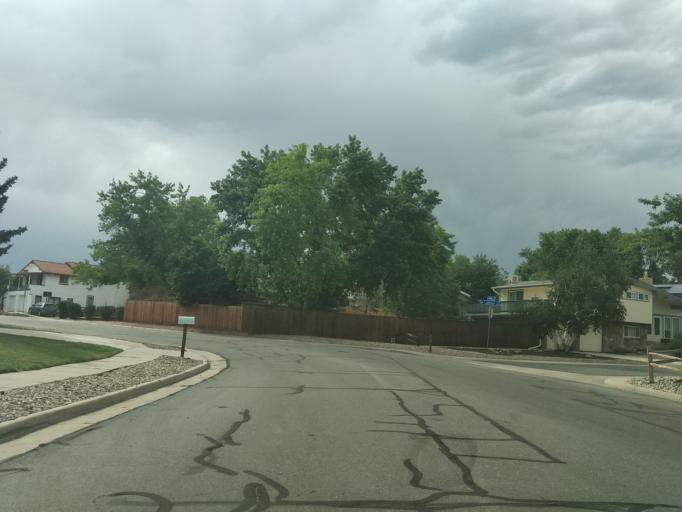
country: US
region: Colorado
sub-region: Jefferson County
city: Lakewood
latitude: 39.7002
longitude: -105.1078
